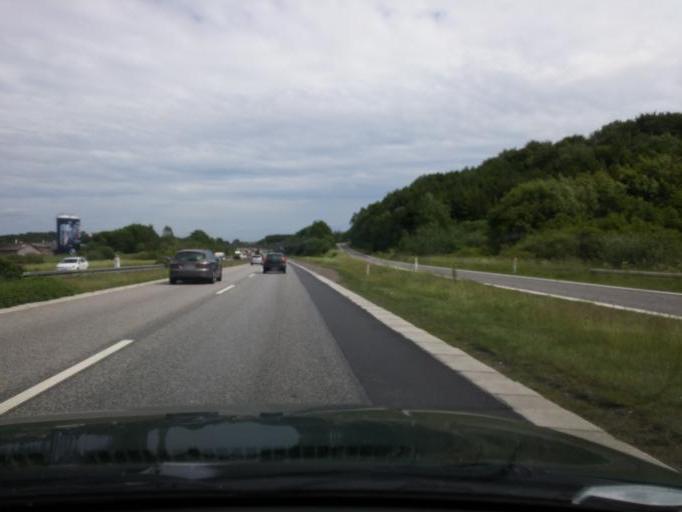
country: DK
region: South Denmark
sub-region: Assens Kommune
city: Vissenbjerg
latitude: 55.4026
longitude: 10.1505
